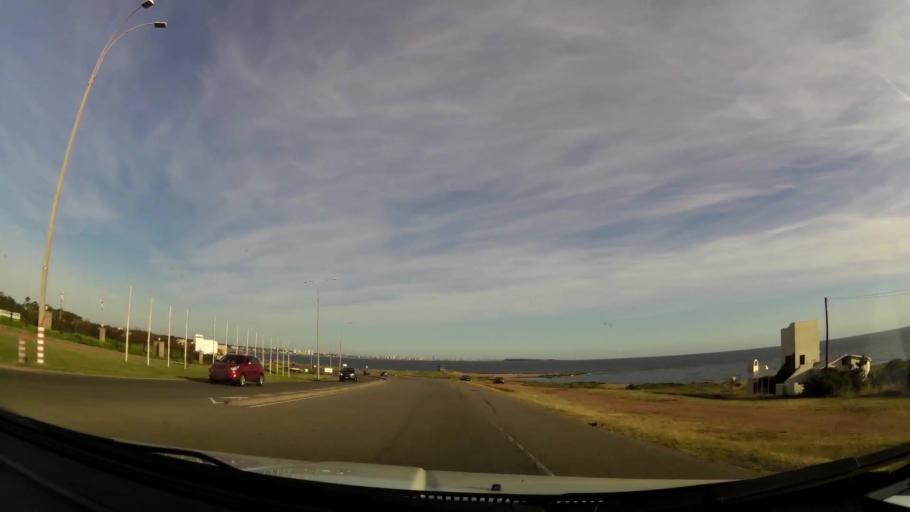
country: UY
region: Maldonado
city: Maldonado
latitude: -34.9087
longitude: -55.0187
